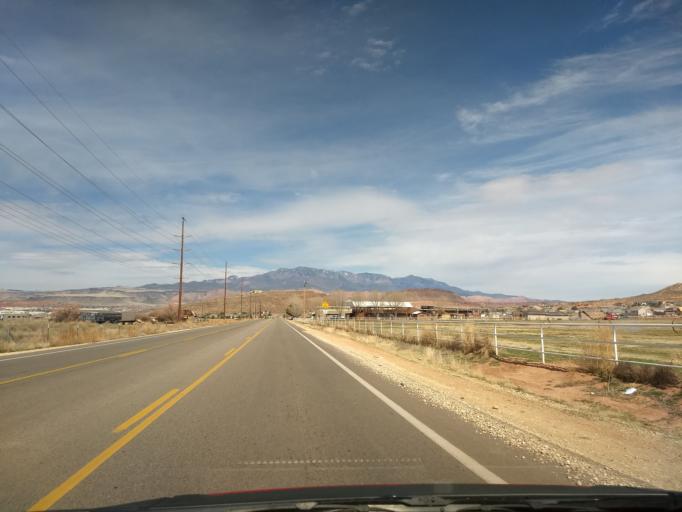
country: US
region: Utah
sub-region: Washington County
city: Washington
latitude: 37.0826
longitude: -113.4996
